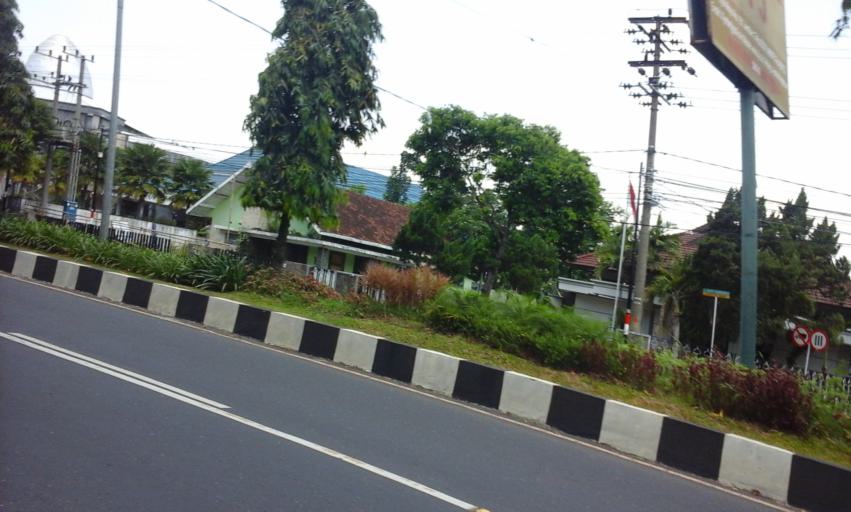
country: ID
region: East Java
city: Kaliwates
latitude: -8.1780
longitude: 113.6802
